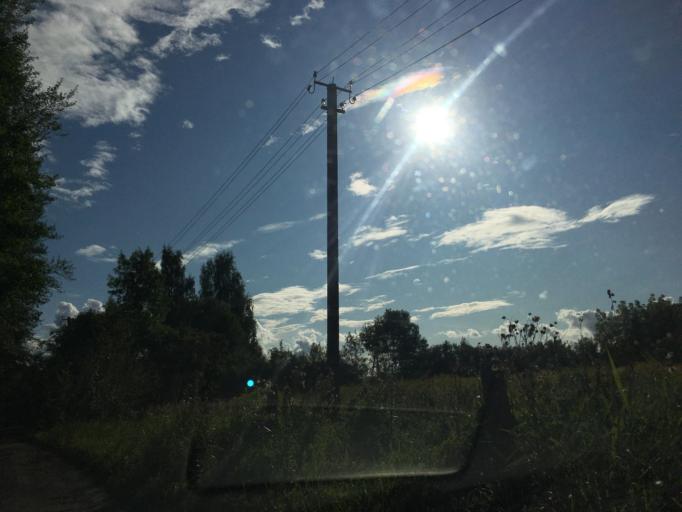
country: RU
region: Pskov
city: Izborsk
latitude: 57.7694
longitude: 27.9748
